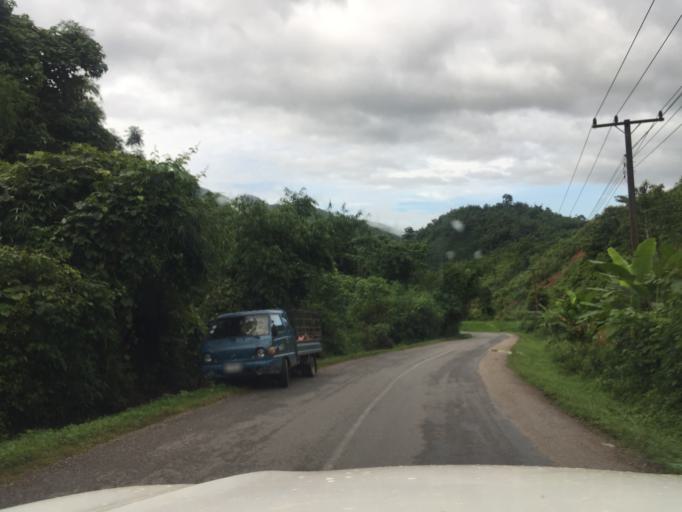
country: LA
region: Oudomxai
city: Muang La
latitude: 20.7998
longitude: 102.0868
